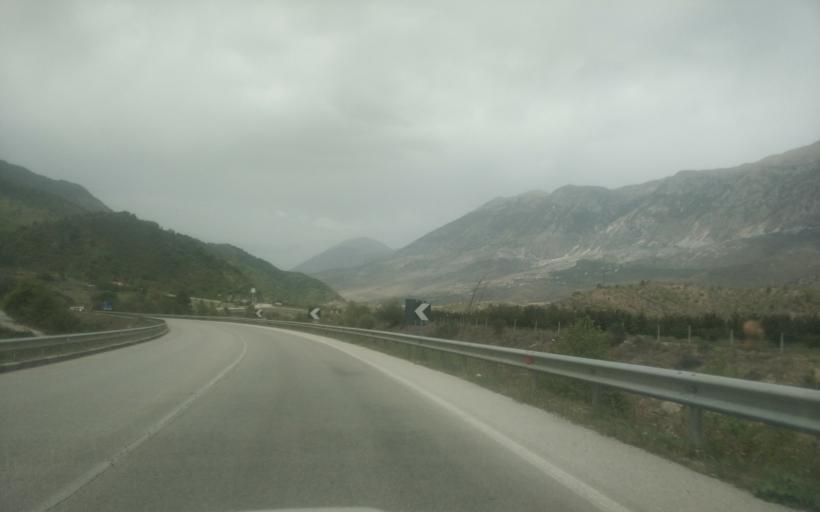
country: AL
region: Gjirokaster
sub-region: Rrethi i Gjirokastres
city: Picar
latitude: 40.2031
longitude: 20.0915
